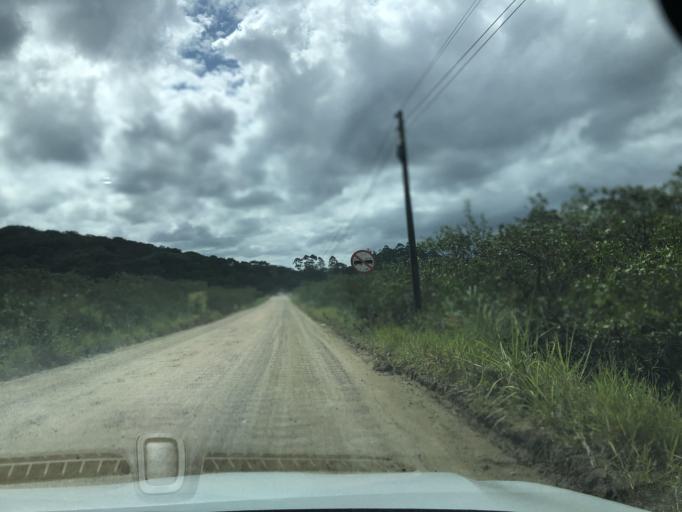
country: BR
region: Santa Catarina
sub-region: Sao Francisco Do Sul
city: Sao Francisco do Sul
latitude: -26.2273
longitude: -48.5915
